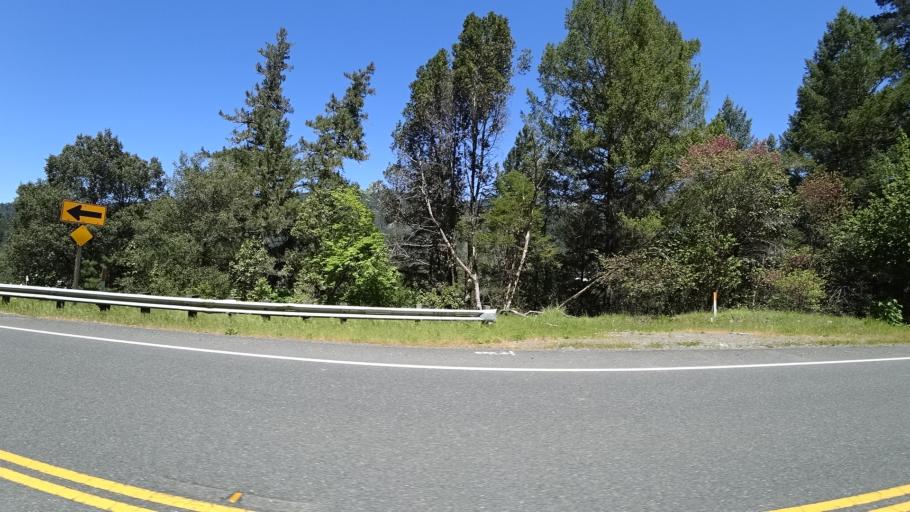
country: US
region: California
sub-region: Humboldt County
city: Willow Creek
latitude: 40.8725
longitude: -123.5298
